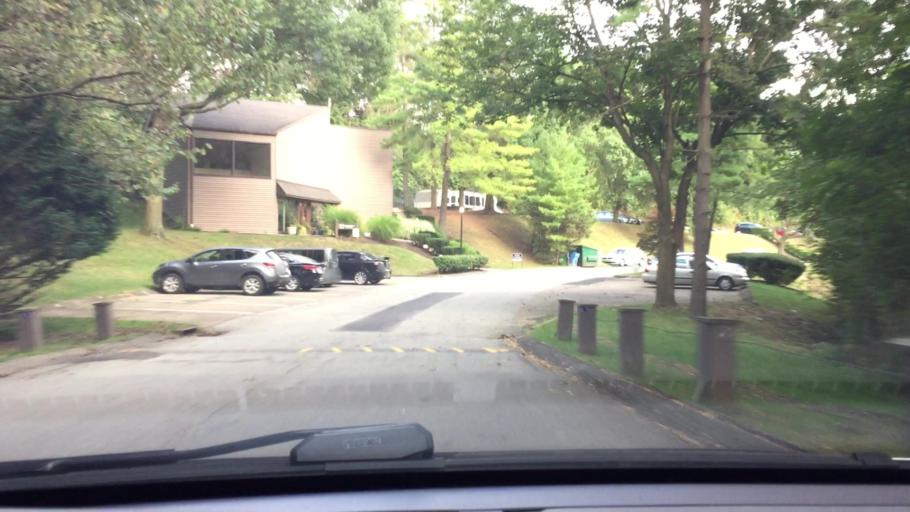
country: US
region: Pennsylvania
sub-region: Allegheny County
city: Green Tree
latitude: 40.3983
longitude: -80.0625
